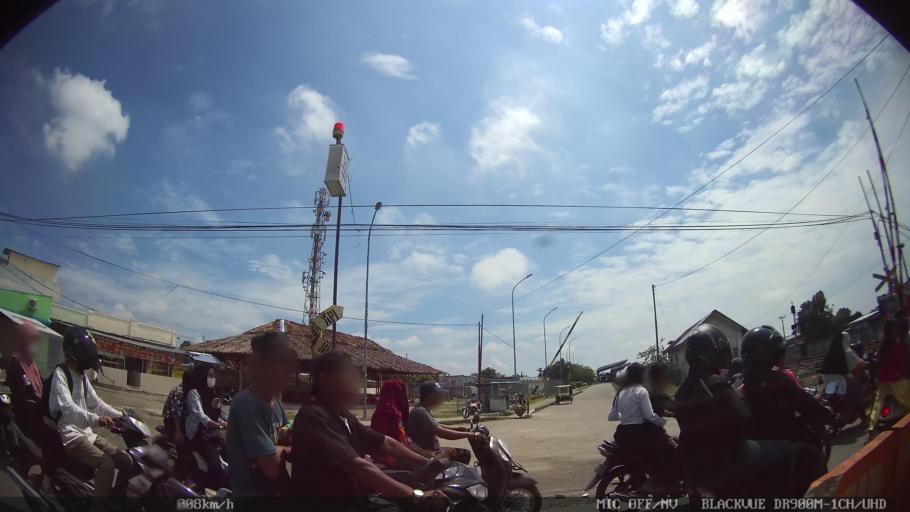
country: ID
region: North Sumatra
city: Medan
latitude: 3.5938
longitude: 98.7545
